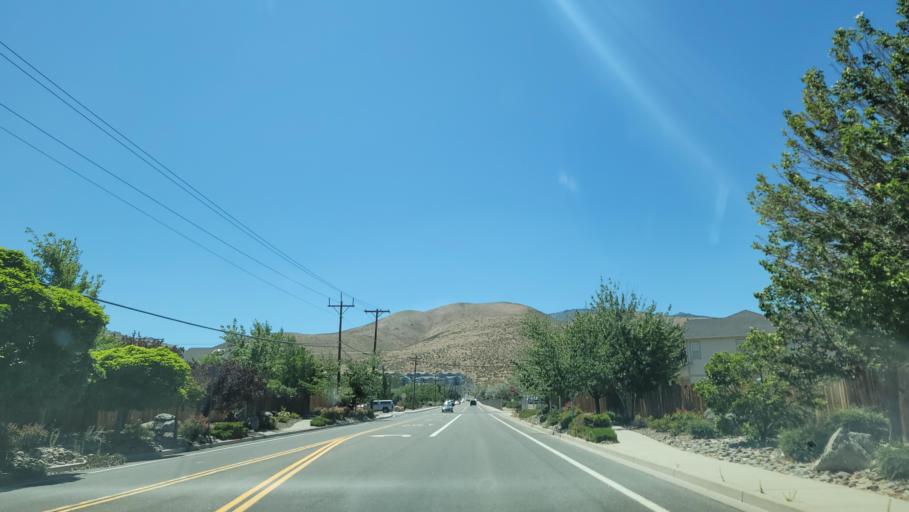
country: US
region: Nevada
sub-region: Carson City
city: Carson City
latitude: 39.1339
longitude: -119.7617
